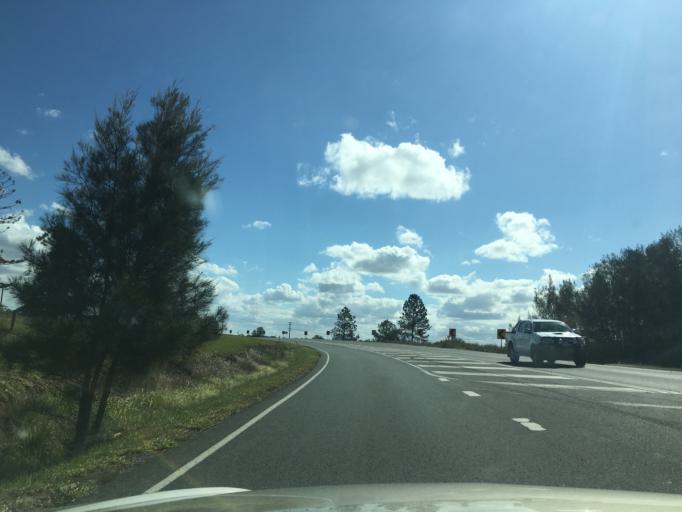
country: AU
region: Queensland
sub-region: Logan
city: Waterford West
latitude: -27.7080
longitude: 153.1340
